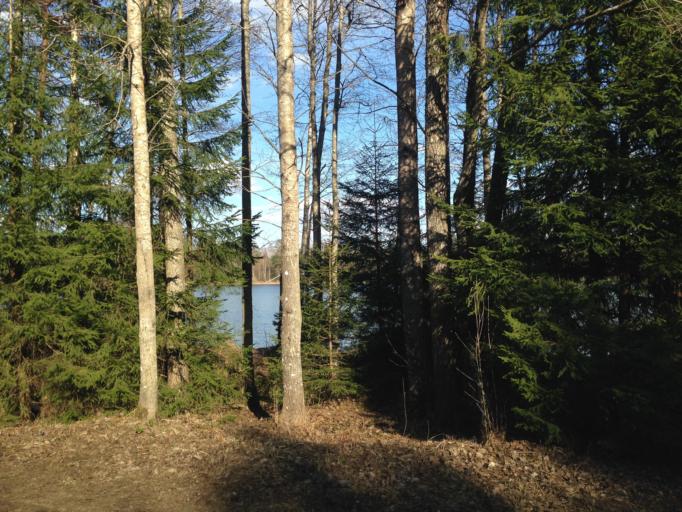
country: EE
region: Harju
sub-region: Nissi vald
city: Turba
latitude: 59.0960
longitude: 24.1520
